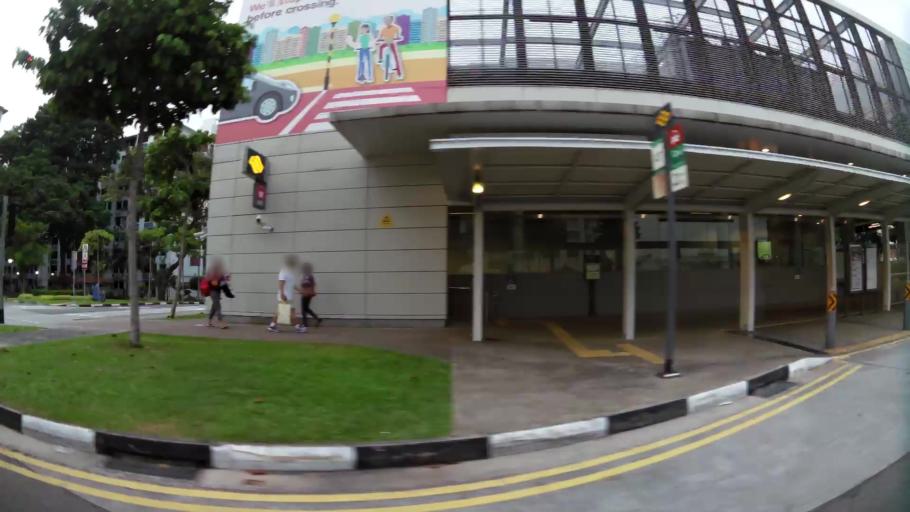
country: SG
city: Singapore
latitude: 1.3086
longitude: 103.8892
